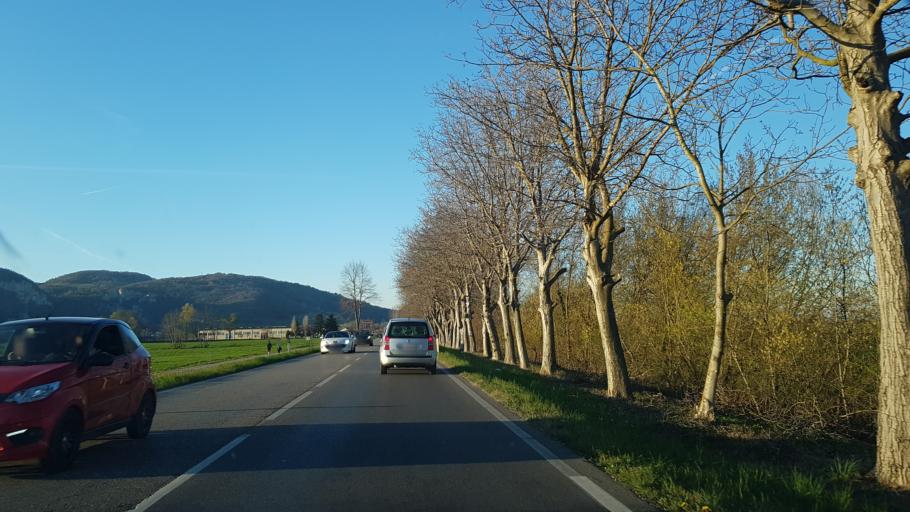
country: IT
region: Veneto
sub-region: Provincia di Vicenza
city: Ponte di Castegnero
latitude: 45.4445
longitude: 11.6010
